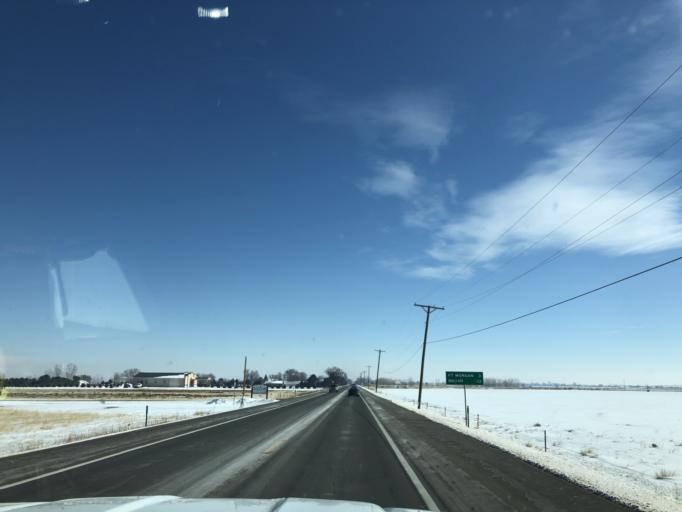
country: US
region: Colorado
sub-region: Morgan County
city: Fort Morgan
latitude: 40.2542
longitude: -103.8735
